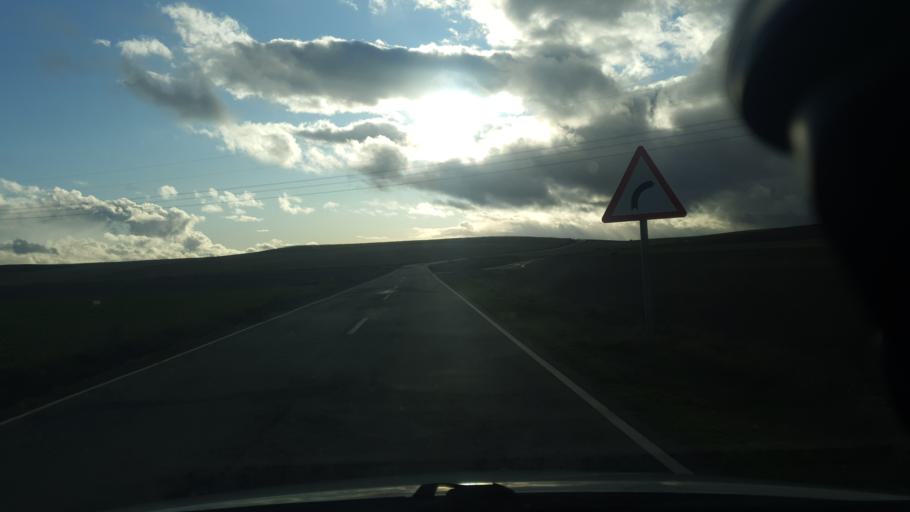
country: ES
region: Castille and Leon
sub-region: Provincia de Segovia
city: Santiuste de San Juan Bautista
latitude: 41.1494
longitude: -4.5786
